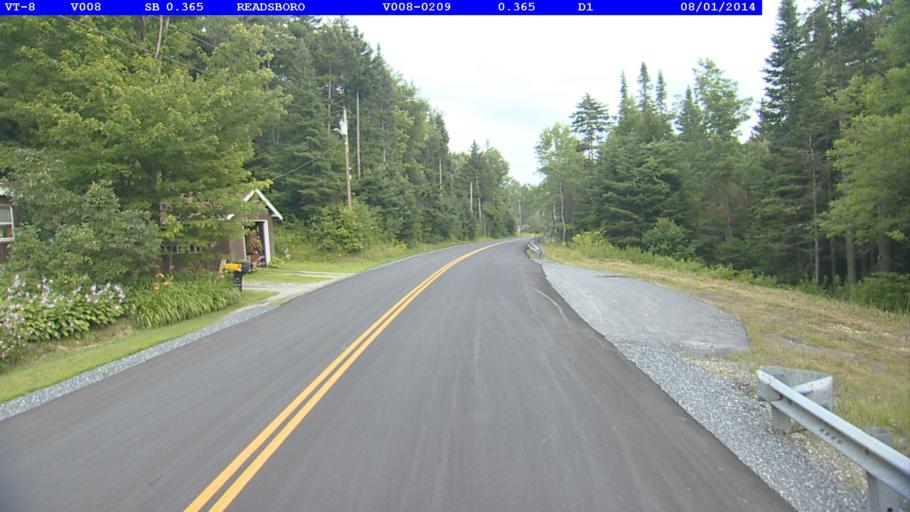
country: US
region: Massachusetts
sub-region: Berkshire County
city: North Adams
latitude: 42.8335
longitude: -72.9896
